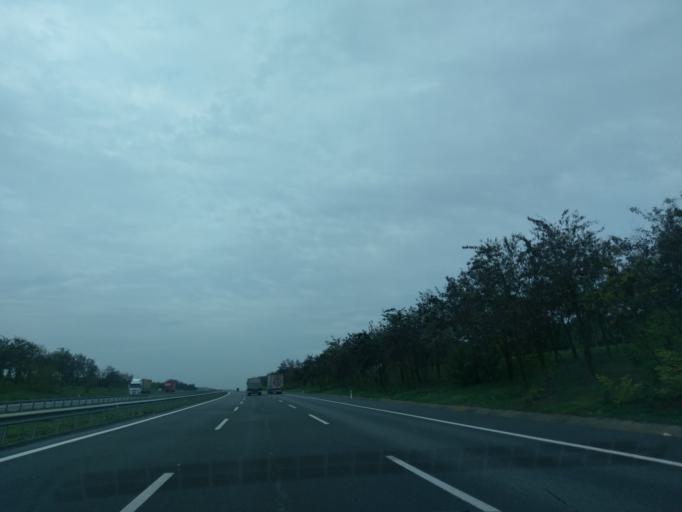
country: TR
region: Istanbul
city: Canta
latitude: 41.1620
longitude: 28.1342
